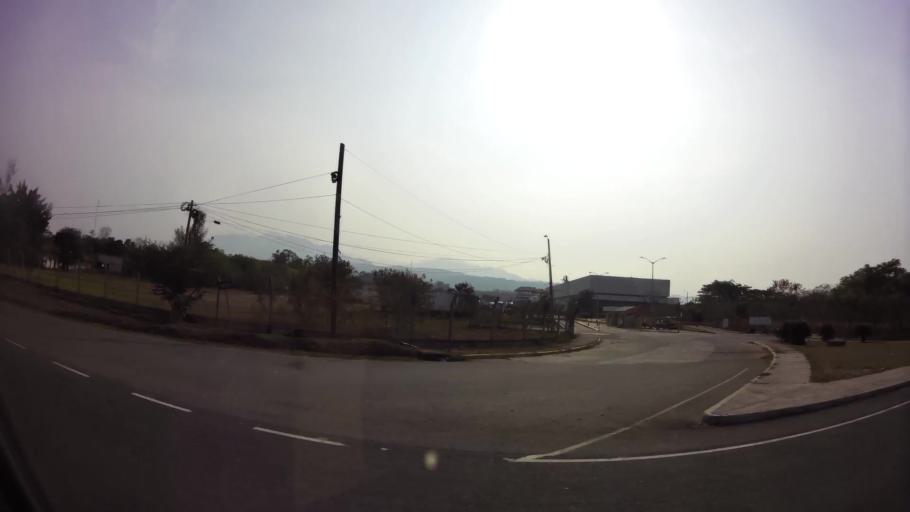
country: HN
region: La Paz
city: Yarumela
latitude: 14.3861
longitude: -87.6119
